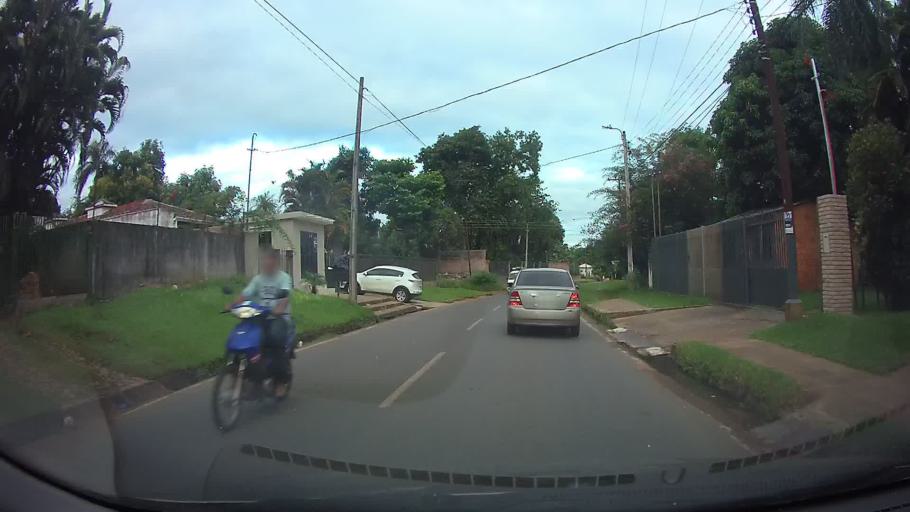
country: PY
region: Central
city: San Lorenzo
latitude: -25.3012
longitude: -57.4983
